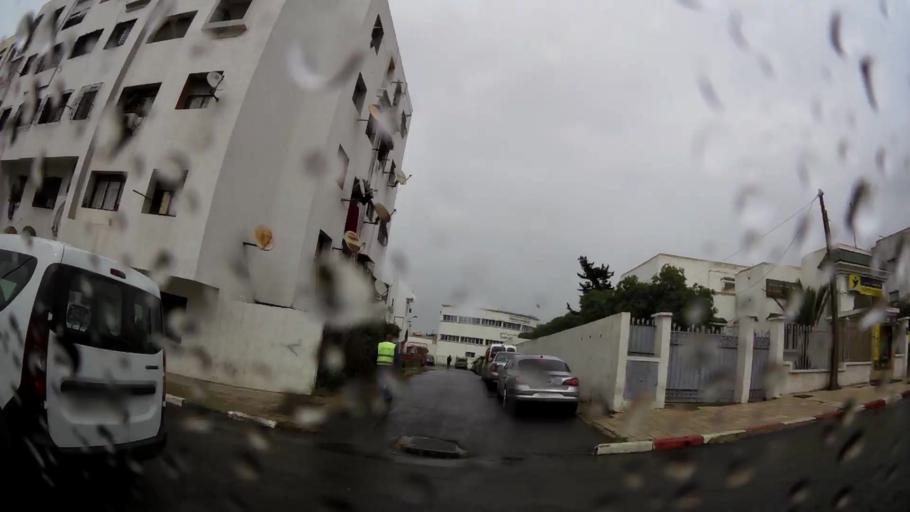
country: MA
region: Grand Casablanca
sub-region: Mediouna
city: Tit Mellil
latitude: 33.6178
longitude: -7.4851
